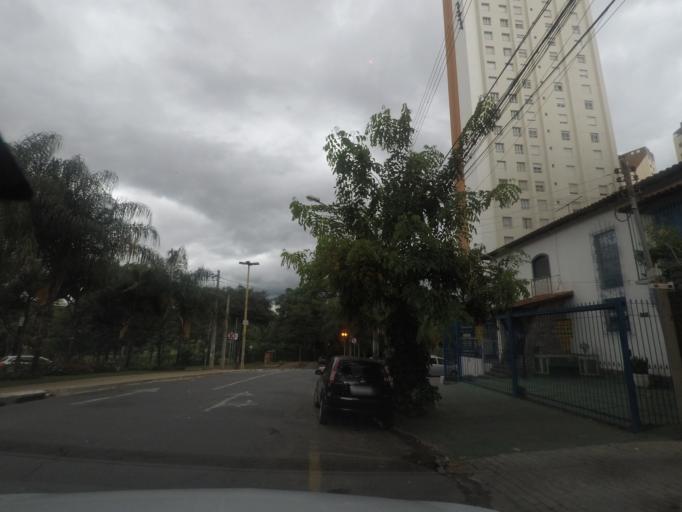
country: BR
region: Goias
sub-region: Goiania
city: Goiania
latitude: -16.6815
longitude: -49.2703
